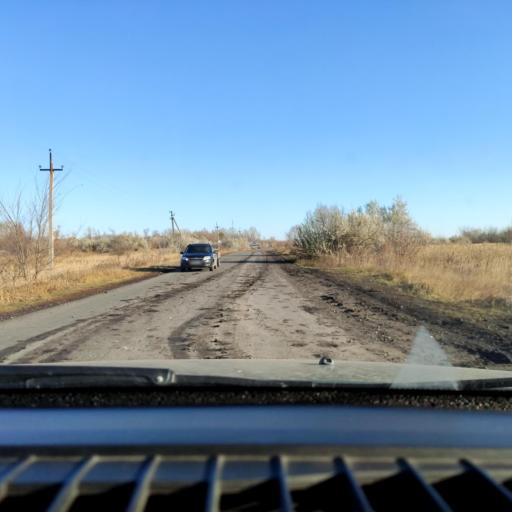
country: RU
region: Samara
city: Tol'yatti
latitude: 53.6362
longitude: 49.3088
